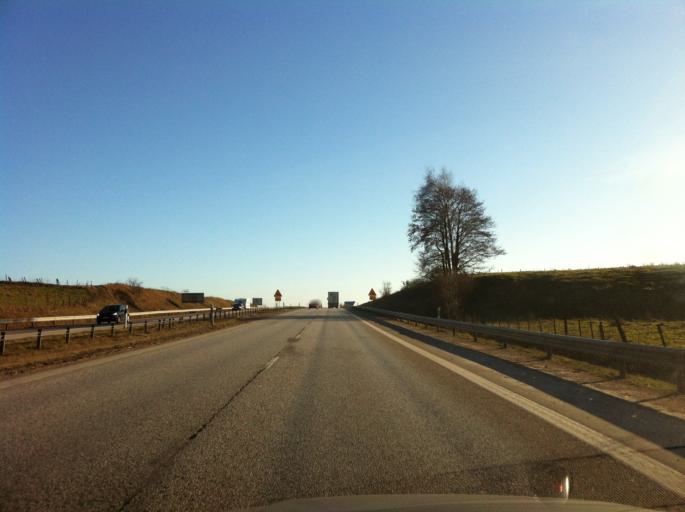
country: SE
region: Skane
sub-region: Angelholms Kommun
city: AEngelholm
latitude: 56.2339
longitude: 12.8985
